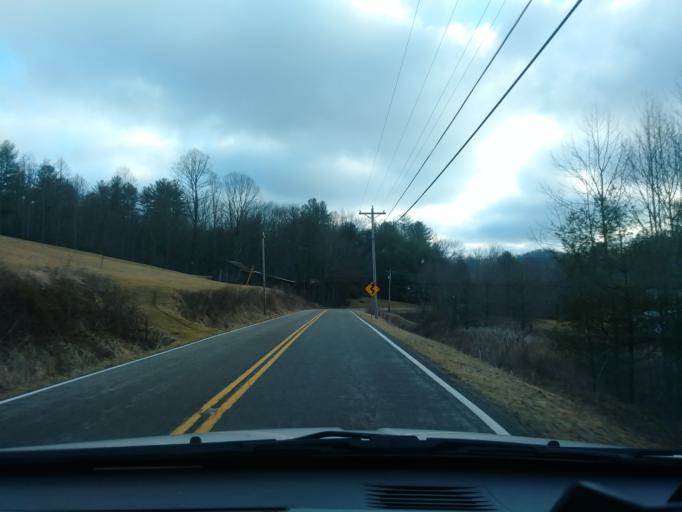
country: US
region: Tennessee
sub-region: Unicoi County
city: Unicoi
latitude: 36.2094
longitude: -82.2303
